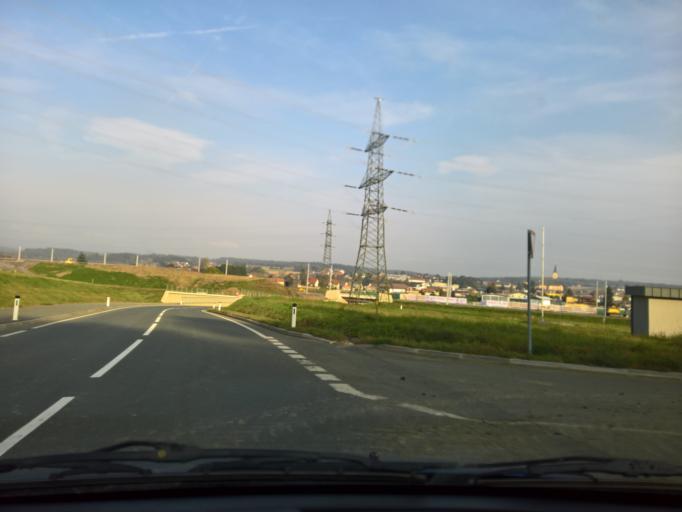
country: AT
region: Styria
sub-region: Politischer Bezirk Deutschlandsberg
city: Gross Sankt Florian
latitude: 46.8135
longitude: 15.3149
